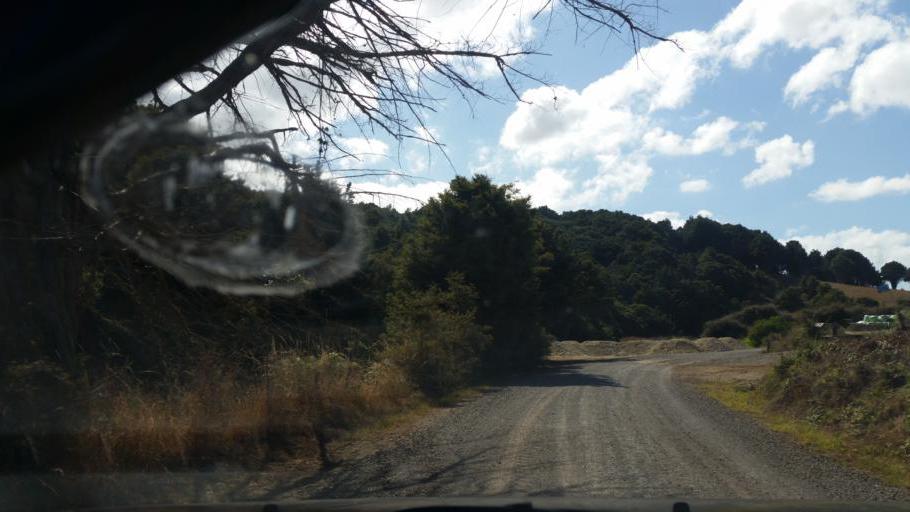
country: NZ
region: Northland
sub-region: Kaipara District
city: Dargaville
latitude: -35.7056
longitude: 173.6006
